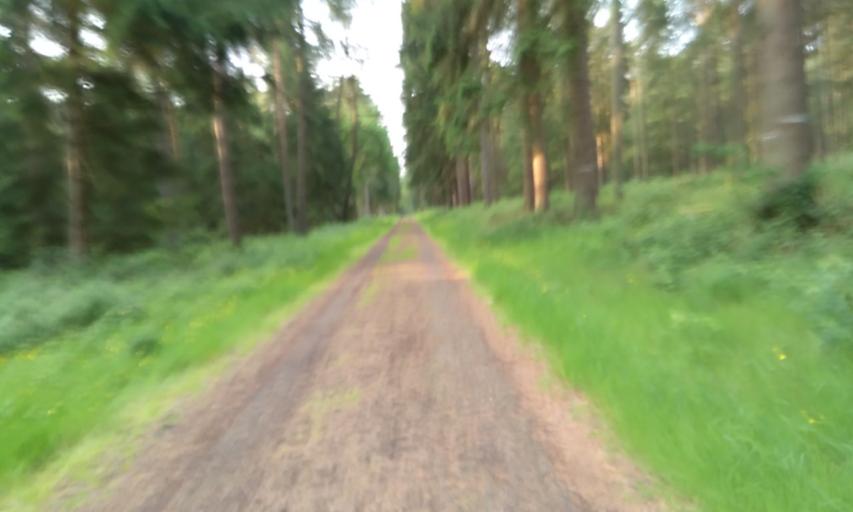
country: DE
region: Lower Saxony
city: Agathenburg
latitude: 53.5273
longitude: 9.5086
